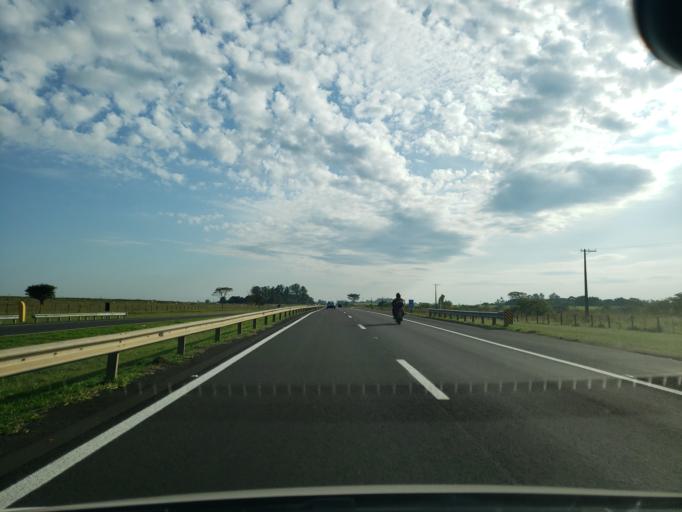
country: BR
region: Sao Paulo
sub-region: Guararapes
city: Guararapes
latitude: -21.2014
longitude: -50.5870
